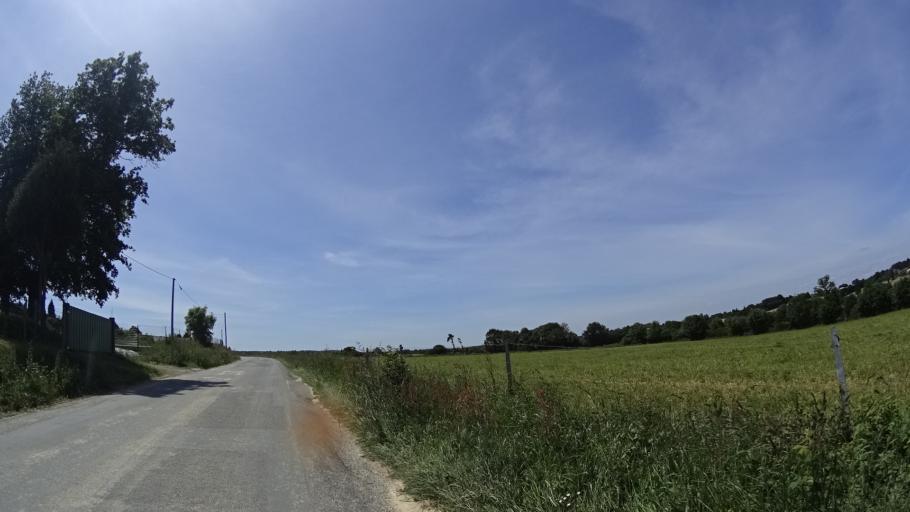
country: FR
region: Brittany
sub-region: Departement d'Ille-et-Vilaine
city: Iffendic
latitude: 48.1350
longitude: -1.9936
